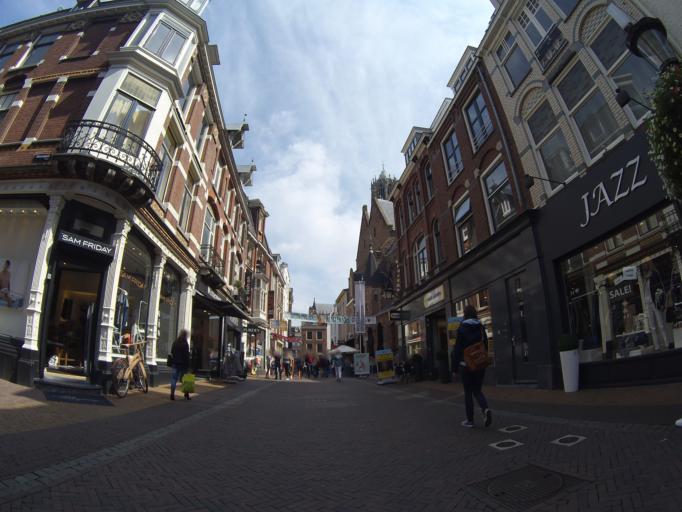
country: NL
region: Utrecht
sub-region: Gemeente Utrecht
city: Utrecht
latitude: 52.0908
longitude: 5.1191
